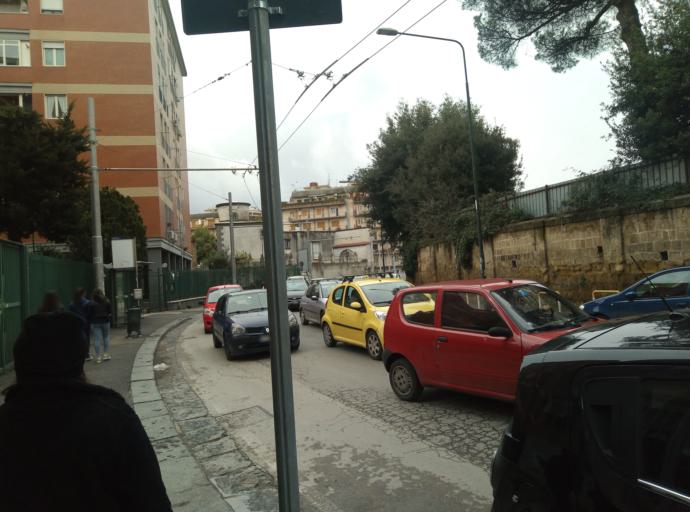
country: IT
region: Campania
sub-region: Provincia di Napoli
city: Napoli
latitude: 40.8622
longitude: 14.2254
